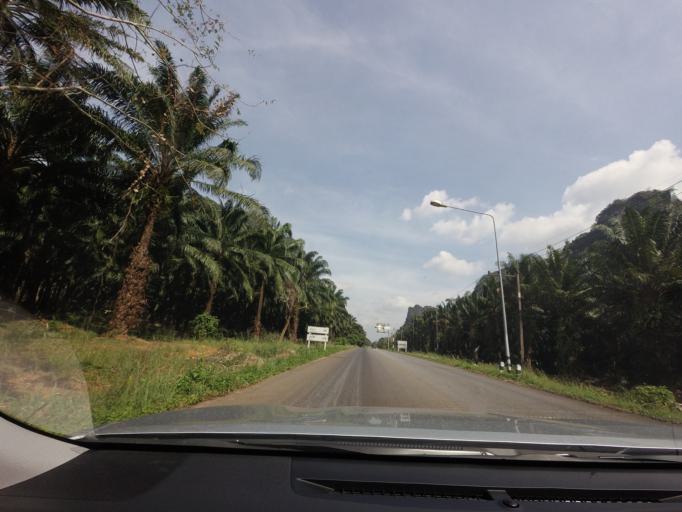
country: TH
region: Phangnga
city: Ban Ao Nang
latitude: 8.1467
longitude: 98.8124
